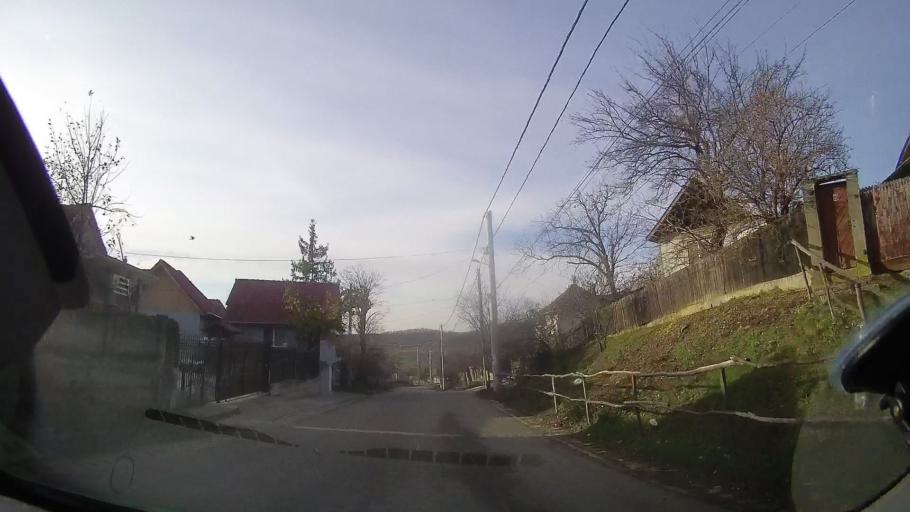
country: RO
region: Bihor
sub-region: Comuna Sarbi
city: Burzuc
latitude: 47.1101
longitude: 22.1753
